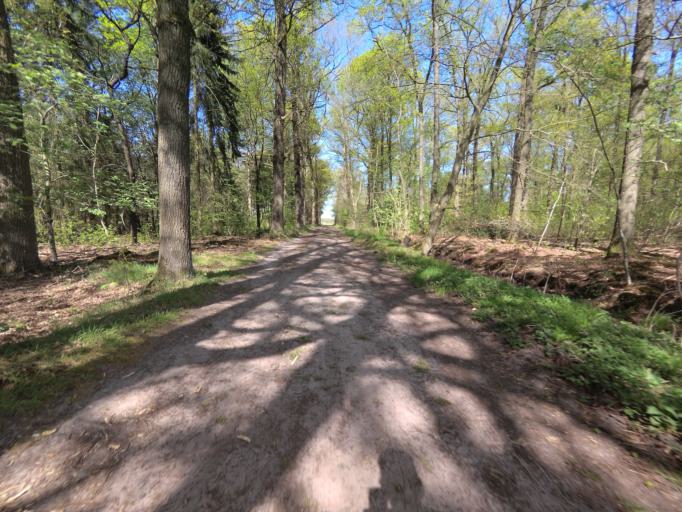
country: NL
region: Utrecht
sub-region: Gemeente Woudenberg
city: Woudenberg
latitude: 52.0909
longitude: 5.4105
